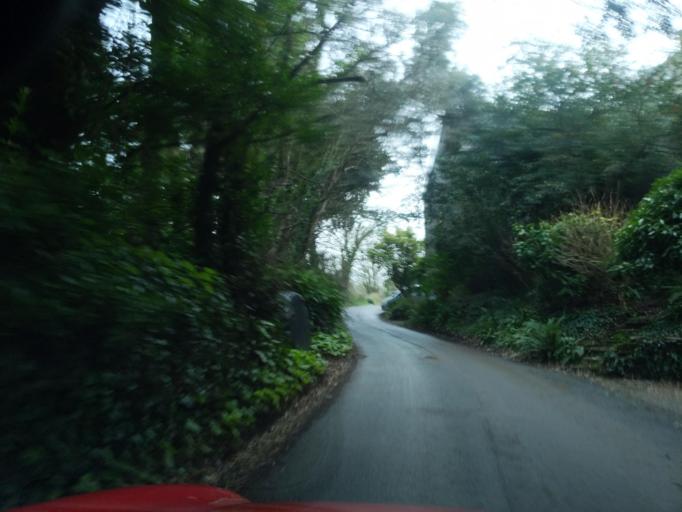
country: GB
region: England
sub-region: Devon
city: Wembury
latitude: 50.3278
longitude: -4.0887
